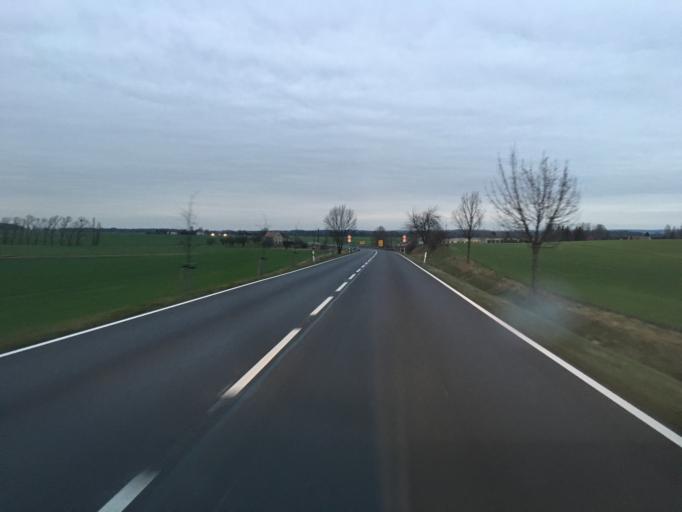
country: DE
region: Saxony
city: Oschatz
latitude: 51.3127
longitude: 13.0822
